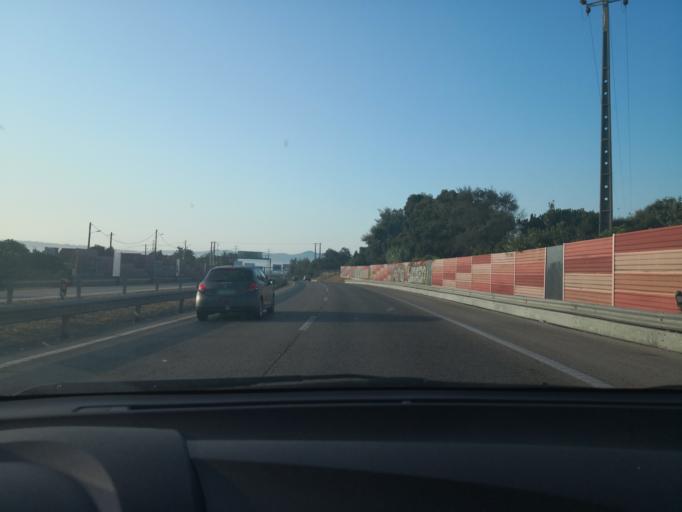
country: PT
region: Setubal
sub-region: Barreiro
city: Santo Antonio da Charneca
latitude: 38.5938
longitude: -9.0210
